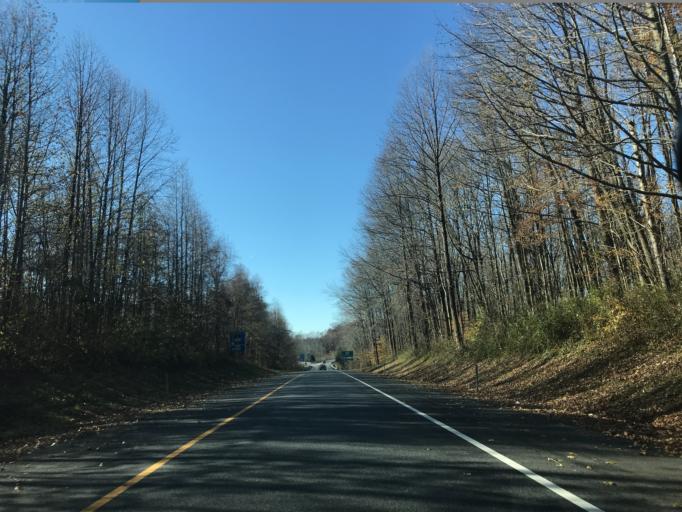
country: US
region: Maryland
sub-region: Harford County
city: Havre de Grace
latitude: 39.5740
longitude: -76.1358
